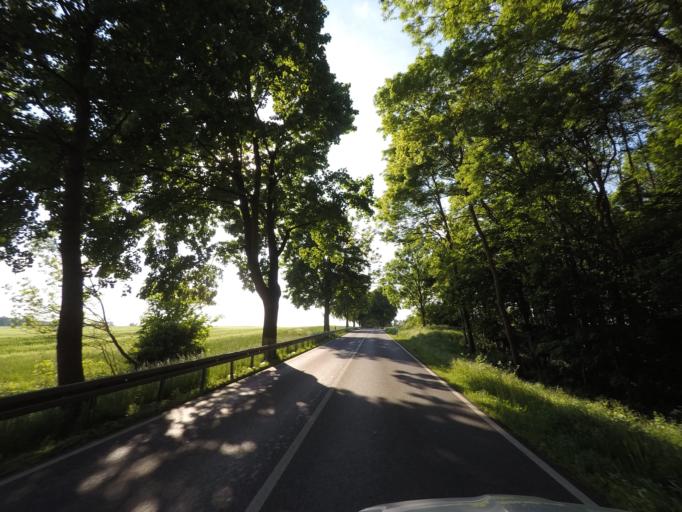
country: DE
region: Brandenburg
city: Hohenfinow
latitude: 52.8147
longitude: 13.9119
